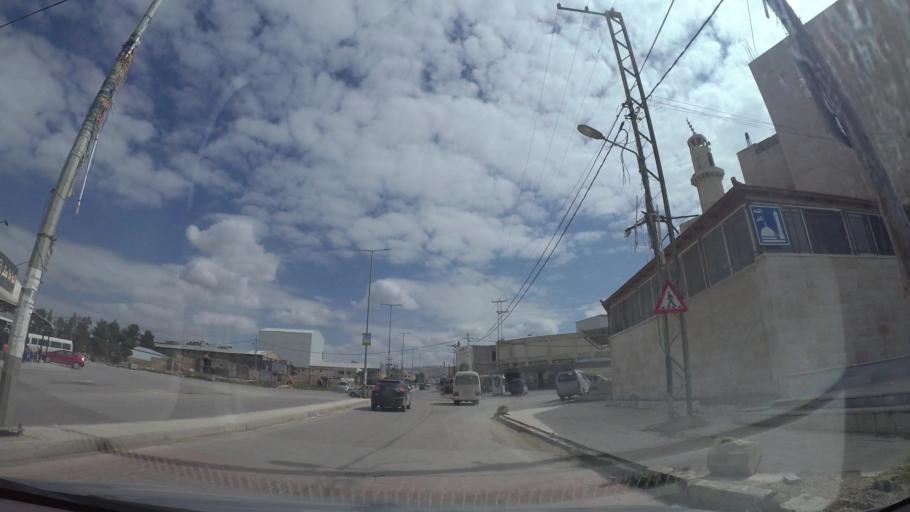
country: JO
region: Amman
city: Al Jubayhah
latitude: 32.0592
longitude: 35.8219
